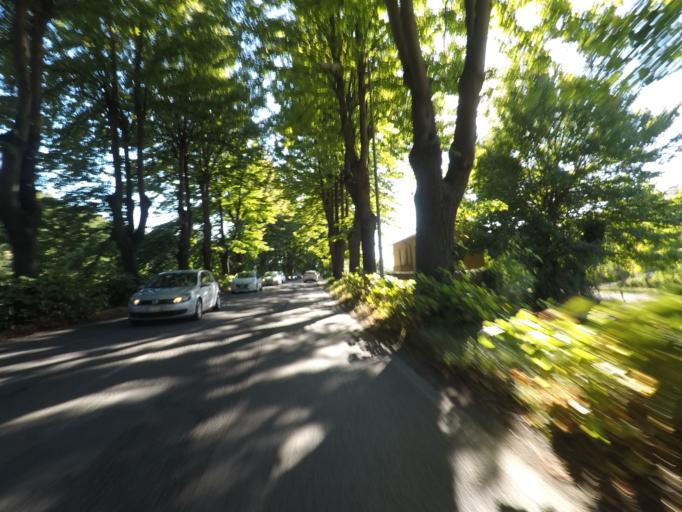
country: IT
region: Tuscany
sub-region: Provincia di Lucca
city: Piano di Mommio
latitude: 43.9327
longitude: 10.2796
